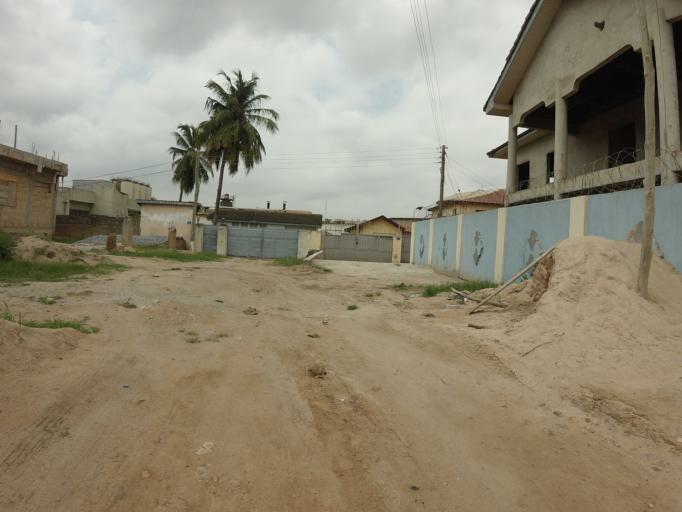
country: GH
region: Greater Accra
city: Dome
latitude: 5.6344
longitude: -0.2367
